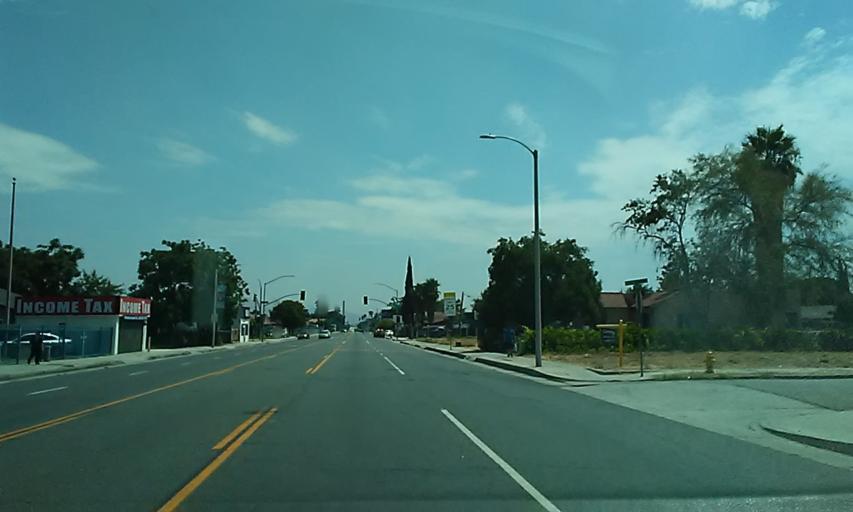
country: US
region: California
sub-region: San Bernardino County
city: San Bernardino
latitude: 34.1188
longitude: -117.3139
